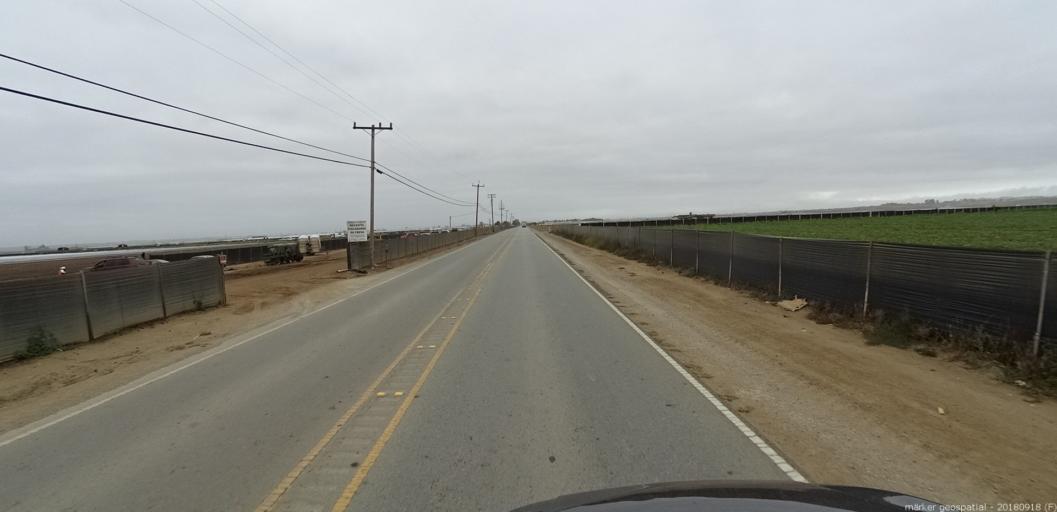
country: US
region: California
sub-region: Monterey County
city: Boronda
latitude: 36.7362
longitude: -121.6625
